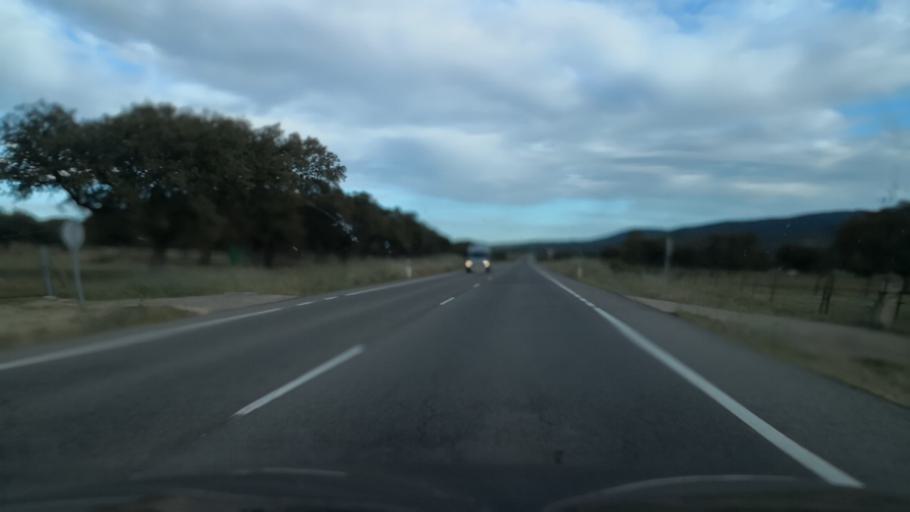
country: ES
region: Extremadura
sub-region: Provincia de Caceres
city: Pedroso de Acim
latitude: 39.8652
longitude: -6.4343
